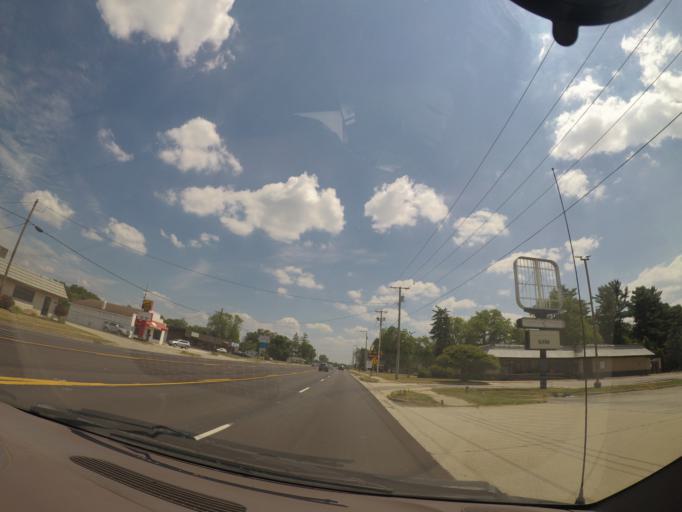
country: US
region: Indiana
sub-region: Elkhart County
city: Dunlap
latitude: 41.6488
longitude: -85.9382
